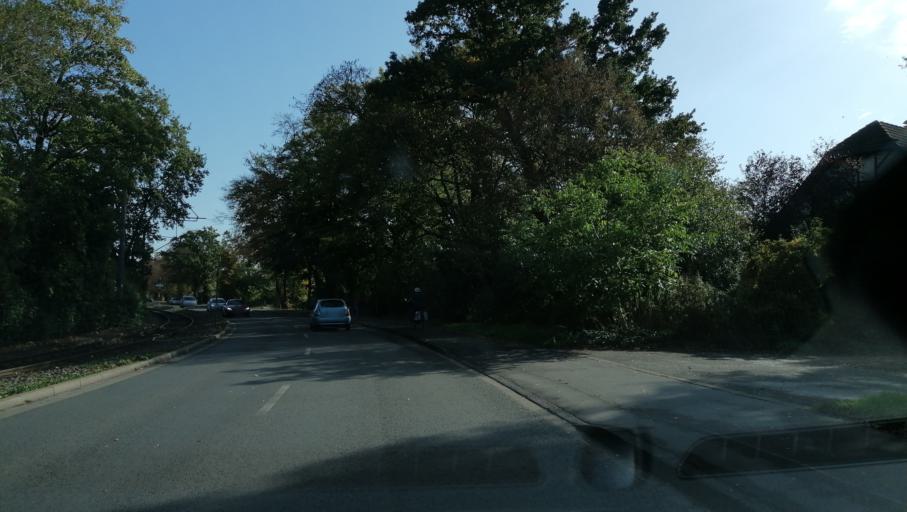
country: DE
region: North Rhine-Westphalia
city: Waltrop
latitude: 51.5877
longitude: 7.4420
